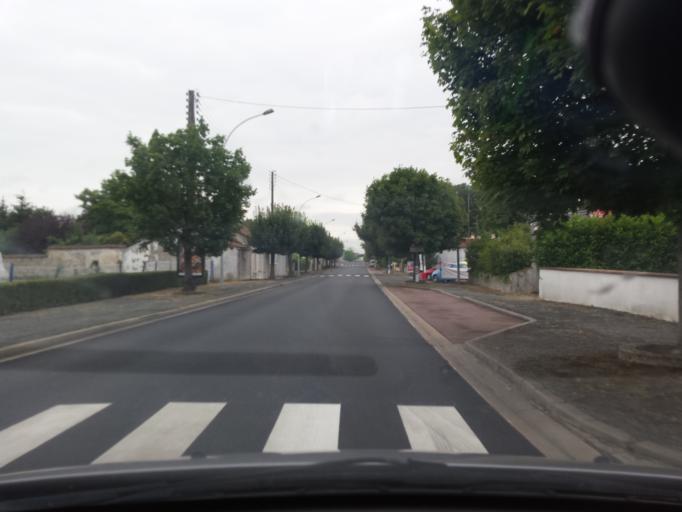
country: FR
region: Pays de la Loire
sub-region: Departement de la Vendee
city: Lucon
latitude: 46.4664
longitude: -1.1734
